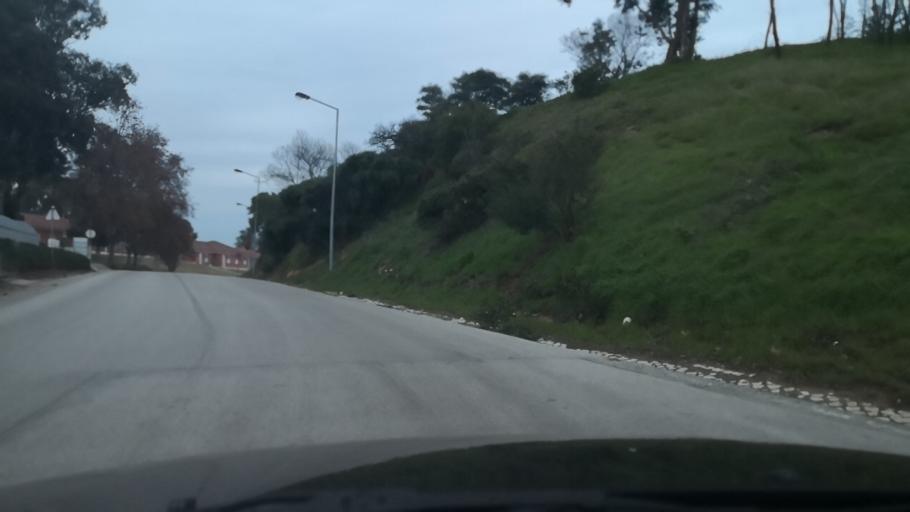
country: PT
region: Setubal
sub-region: Setubal
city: Setubal
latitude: 38.4957
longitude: -8.8325
